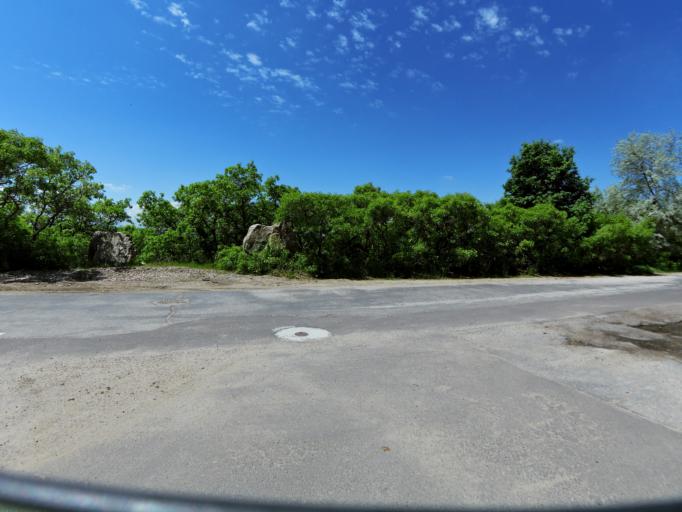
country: US
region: Utah
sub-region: Weber County
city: Uintah
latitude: 41.1630
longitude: -111.9178
